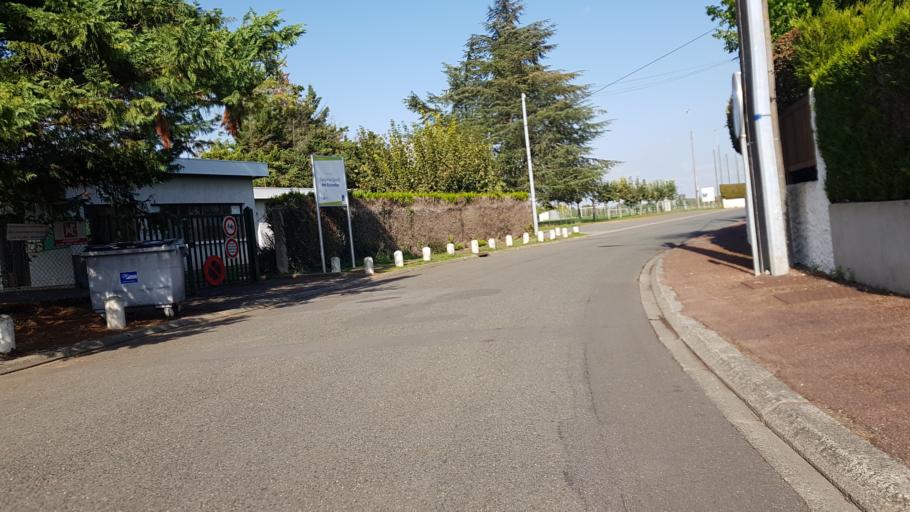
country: FR
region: Poitou-Charentes
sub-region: Departement de la Vienne
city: Chasseneuil-du-Poitou
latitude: 46.6570
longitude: 0.3784
